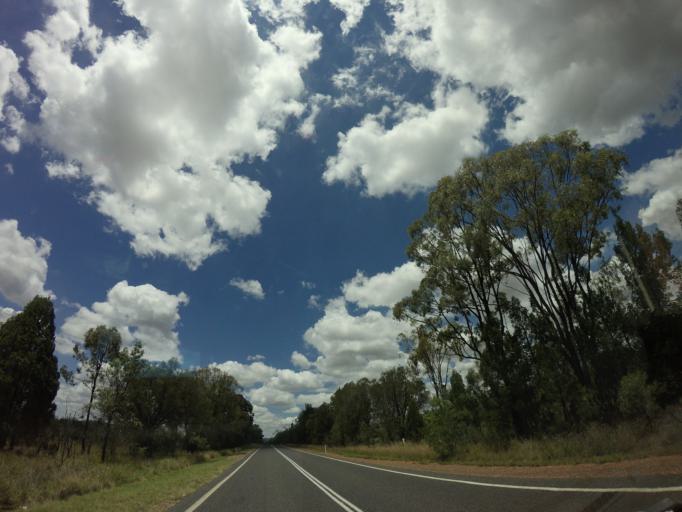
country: AU
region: Queensland
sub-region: Western Downs
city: Dalby
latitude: -27.9645
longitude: 151.1169
